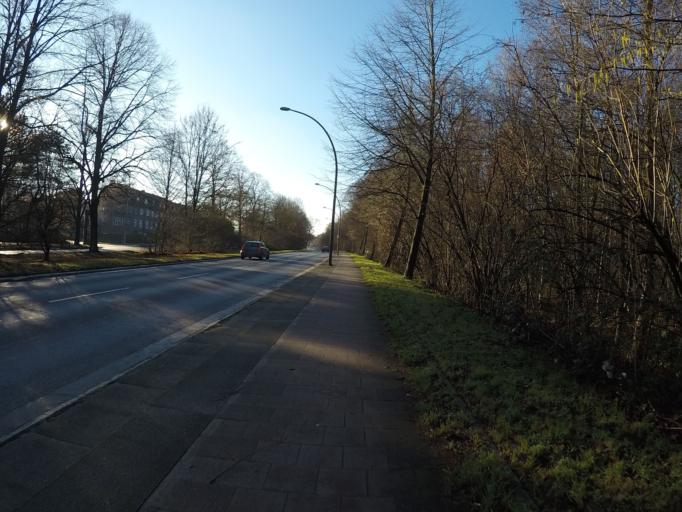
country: DE
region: Hamburg
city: Winterhude
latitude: 53.6065
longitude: 9.9902
